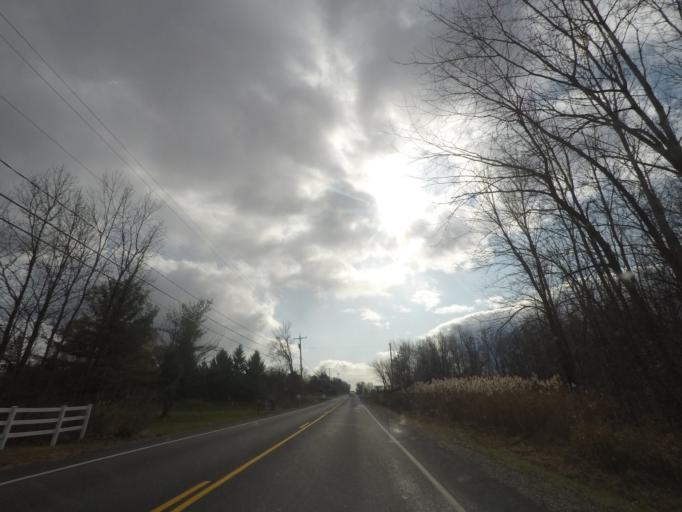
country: US
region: New York
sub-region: Saratoga County
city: Ballston Spa
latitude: 42.9655
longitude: -73.8301
